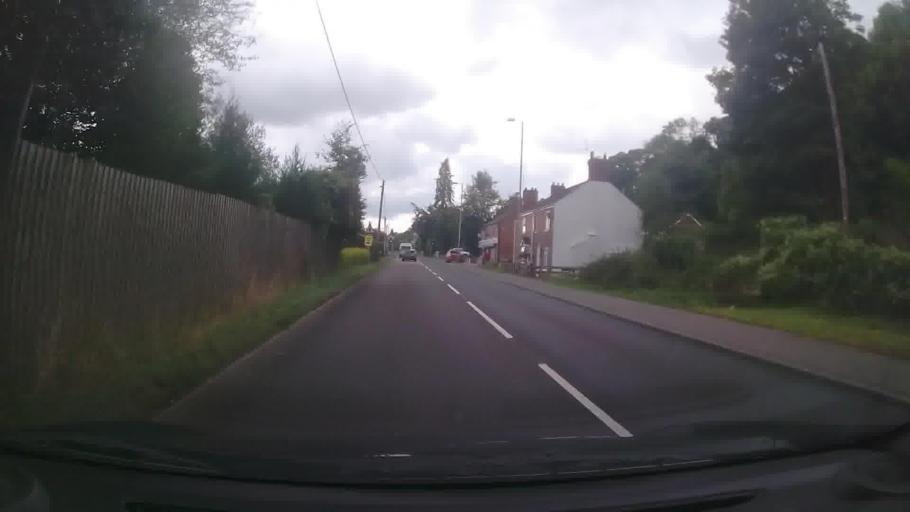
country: GB
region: England
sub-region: Shropshire
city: Pant
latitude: 52.7971
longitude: -3.0749
